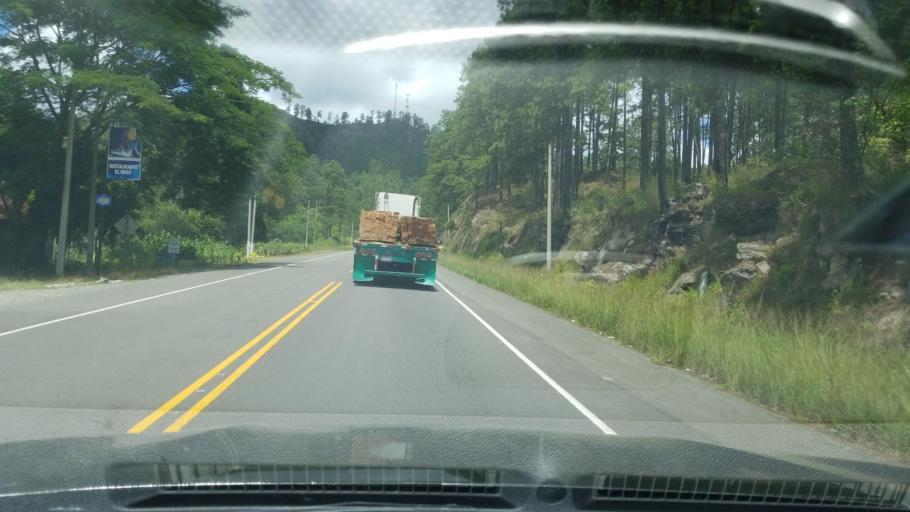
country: HN
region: Francisco Morazan
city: Talanga
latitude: 14.3961
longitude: -87.1274
